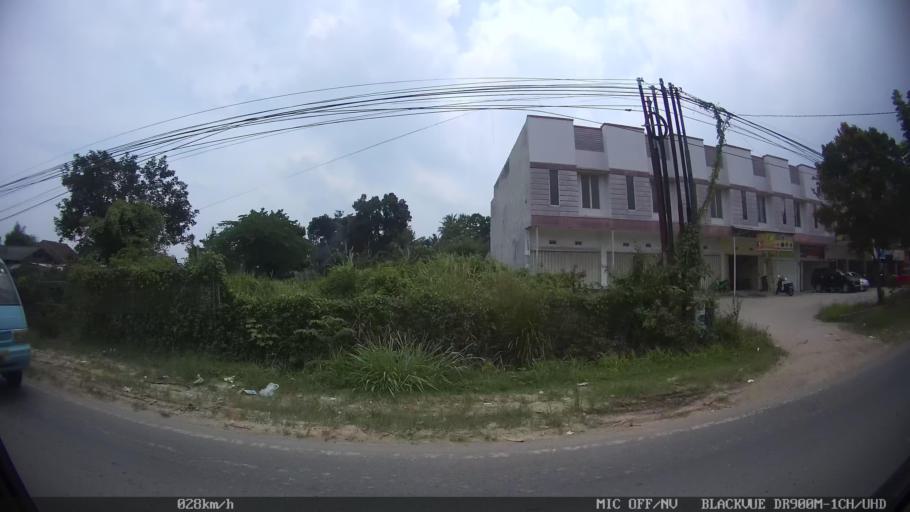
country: ID
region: Lampung
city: Kedaton
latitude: -5.4019
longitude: 105.3143
